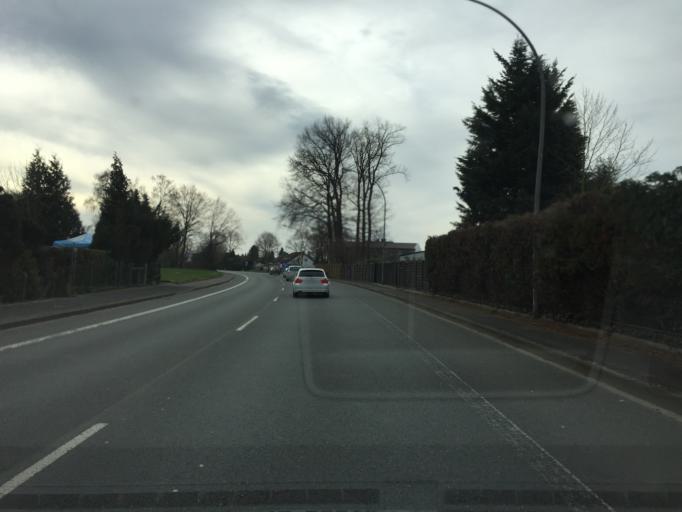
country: DE
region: North Rhine-Westphalia
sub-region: Regierungsbezirk Detmold
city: Lage
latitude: 52.0305
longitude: 8.7567
